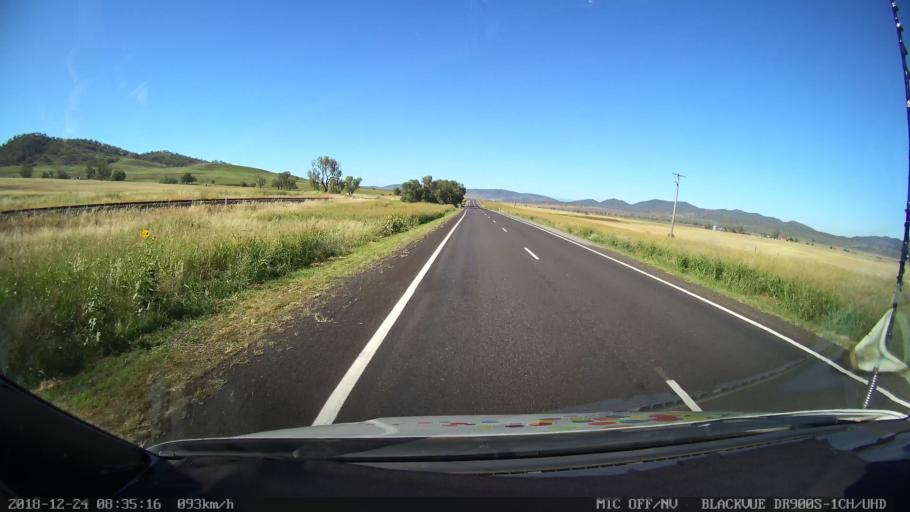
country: AU
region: New South Wales
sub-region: Liverpool Plains
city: Quirindi
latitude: -31.3004
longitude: 150.6606
